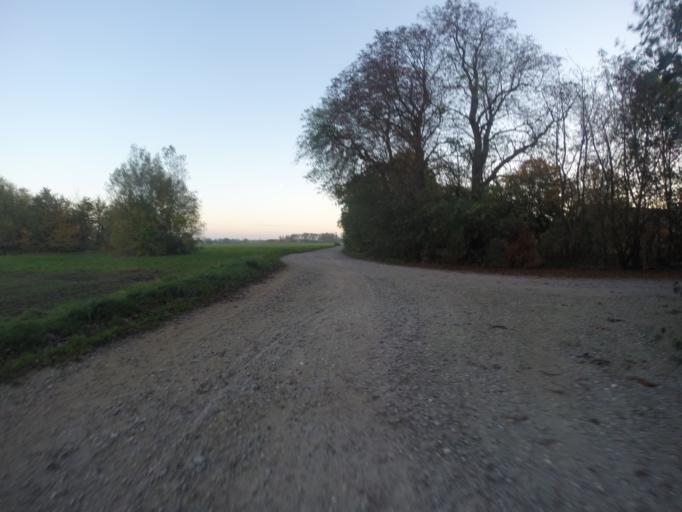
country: DK
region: Capital Region
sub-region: Hoje-Taastrup Kommune
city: Taastrup
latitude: 55.6800
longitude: 12.2933
